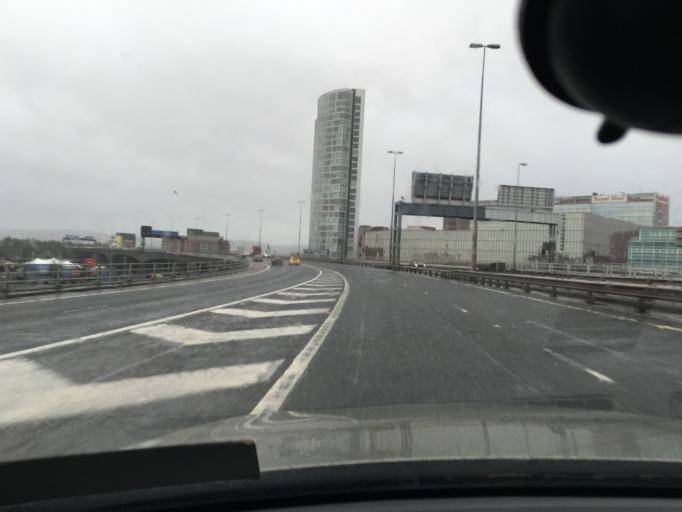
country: GB
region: Northern Ireland
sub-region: City of Belfast
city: Belfast
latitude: 54.6048
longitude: -5.9235
